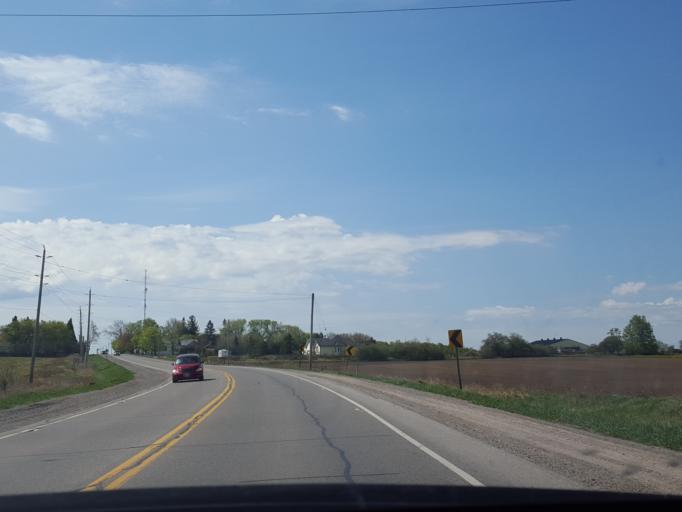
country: CA
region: Ontario
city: Uxbridge
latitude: 44.1171
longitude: -78.9215
